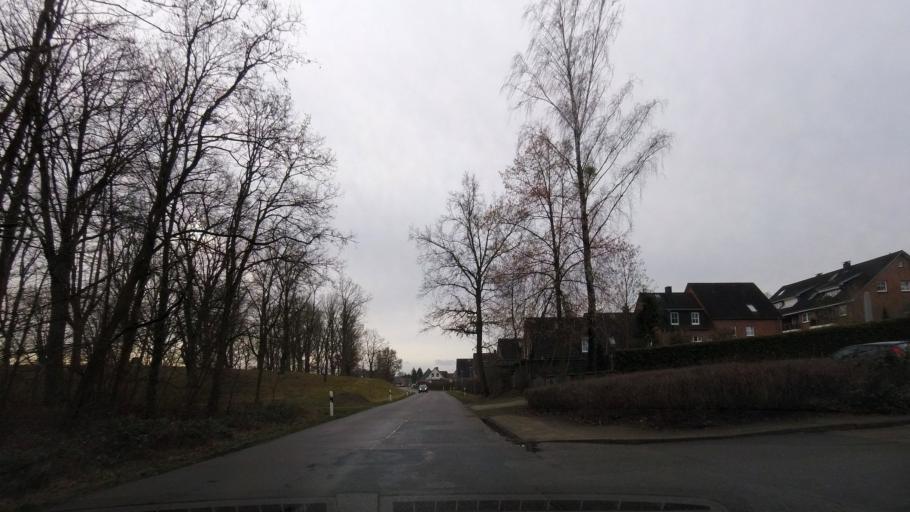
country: DE
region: Mecklenburg-Vorpommern
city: Waren
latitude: 53.5316
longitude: 12.6855
